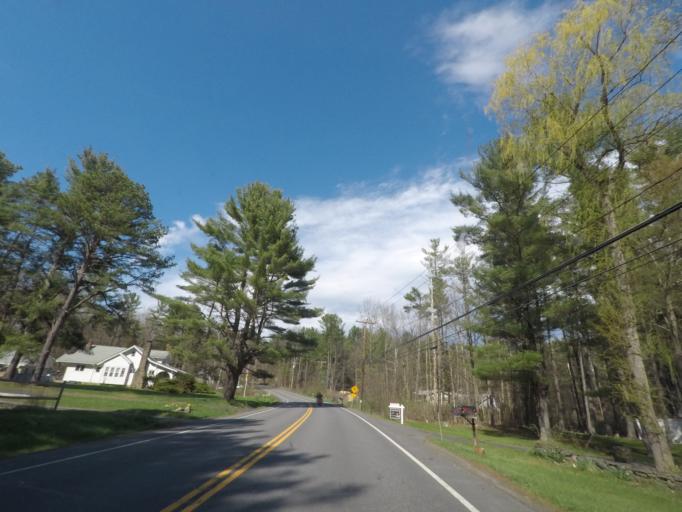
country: US
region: New York
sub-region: Greene County
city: Cairo
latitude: 42.3631
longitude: -74.0437
